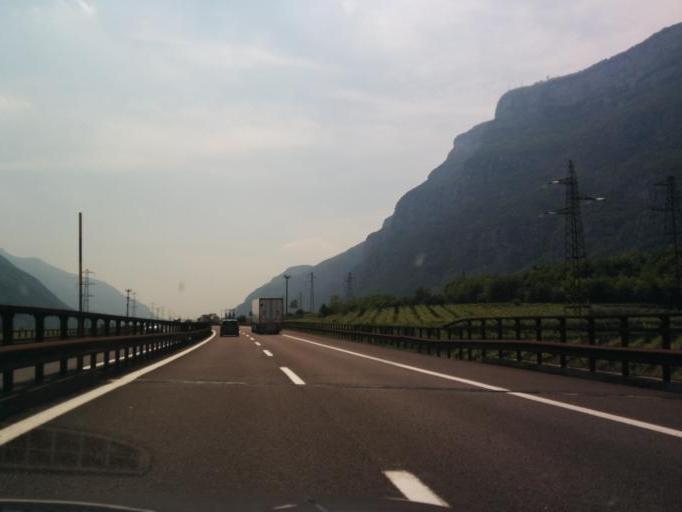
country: IT
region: Veneto
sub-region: Provincia di Verona
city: Rivalta
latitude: 45.6428
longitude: 10.8806
